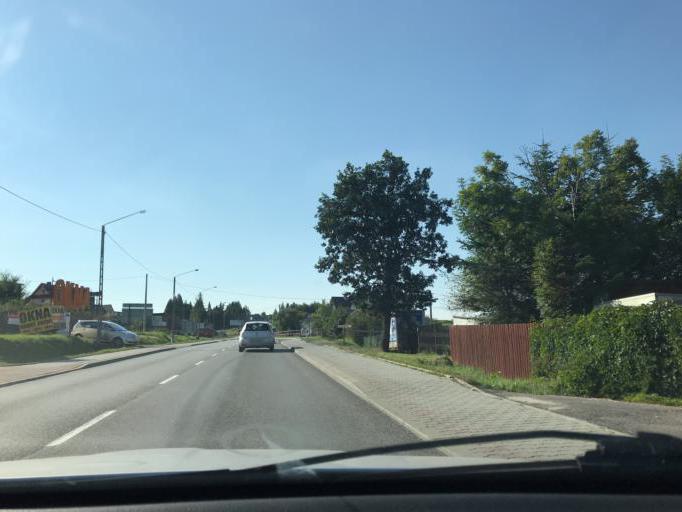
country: PL
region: Lesser Poland Voivodeship
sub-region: Powiat nowotarski
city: Nowy Targ
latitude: 49.4932
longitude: 20.0108
